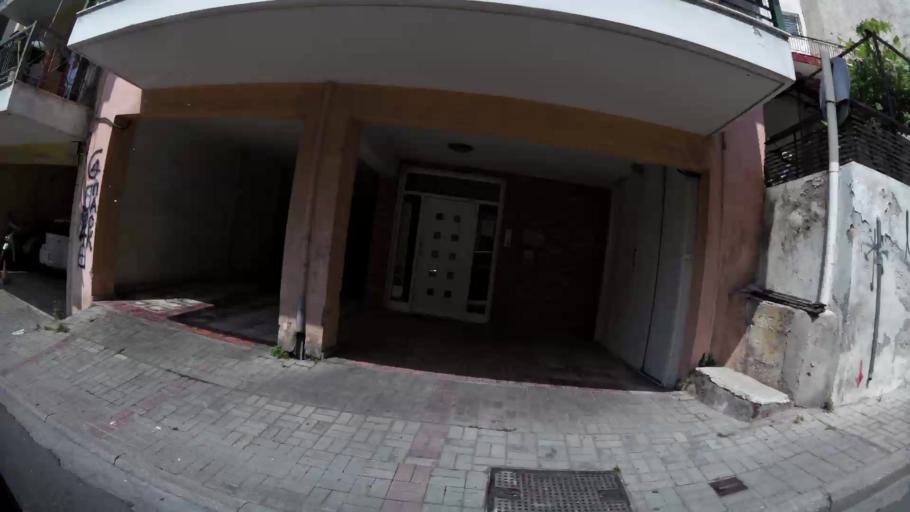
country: GR
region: Central Macedonia
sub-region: Nomos Thessalonikis
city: Sykies
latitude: 40.6460
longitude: 22.9550
